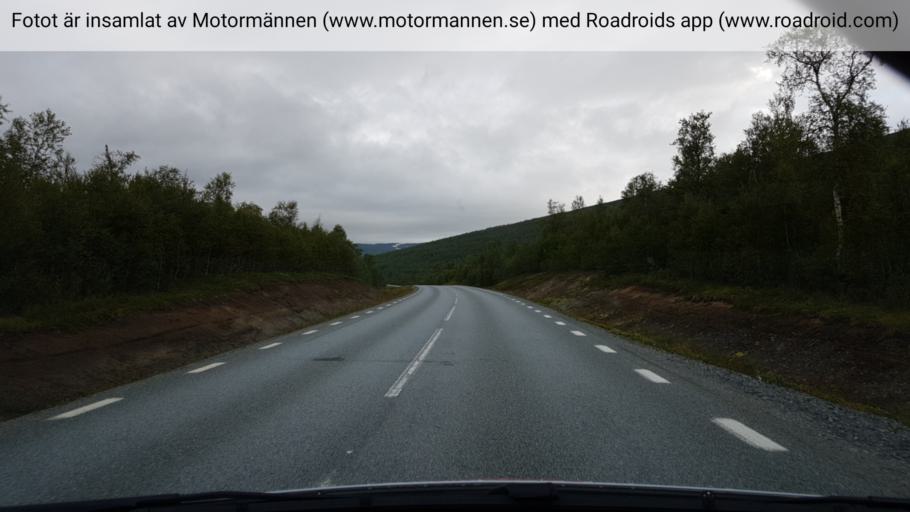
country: NO
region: Nordland
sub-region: Rana
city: Mo i Rana
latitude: 66.0668
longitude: 14.8742
